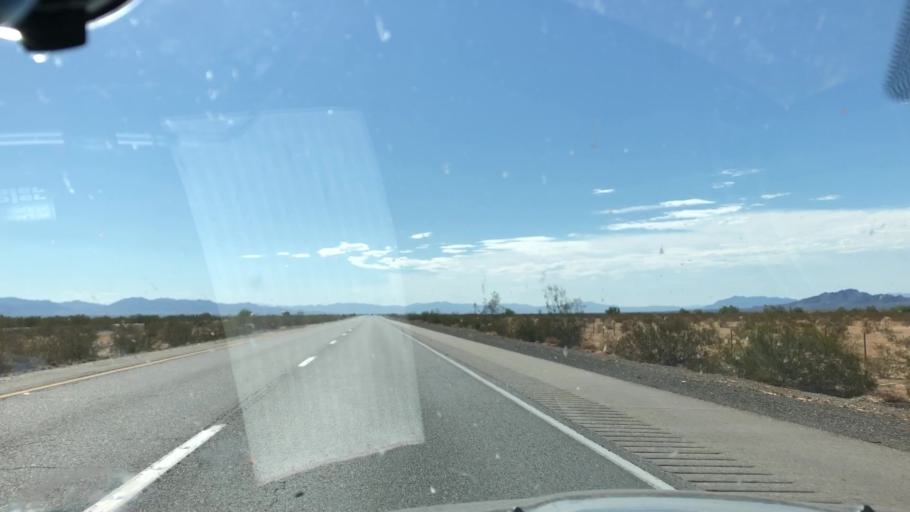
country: US
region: California
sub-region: Riverside County
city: Mesa Verde
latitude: 33.6150
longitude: -115.0148
